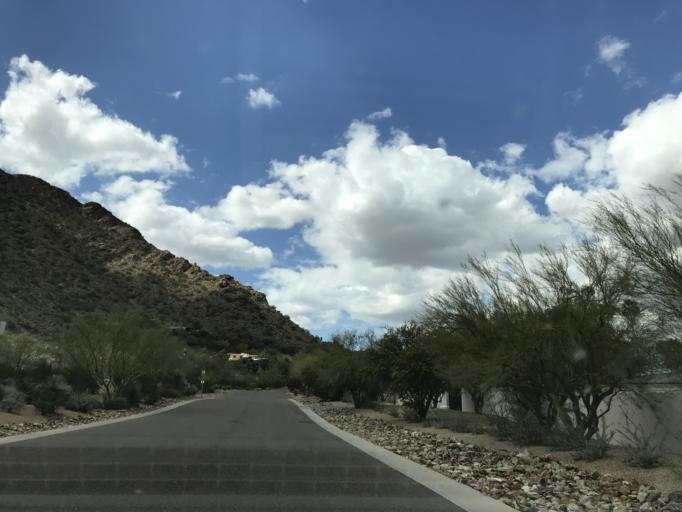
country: US
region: Arizona
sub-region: Maricopa County
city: Paradise Valley
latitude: 33.5190
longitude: -111.9507
